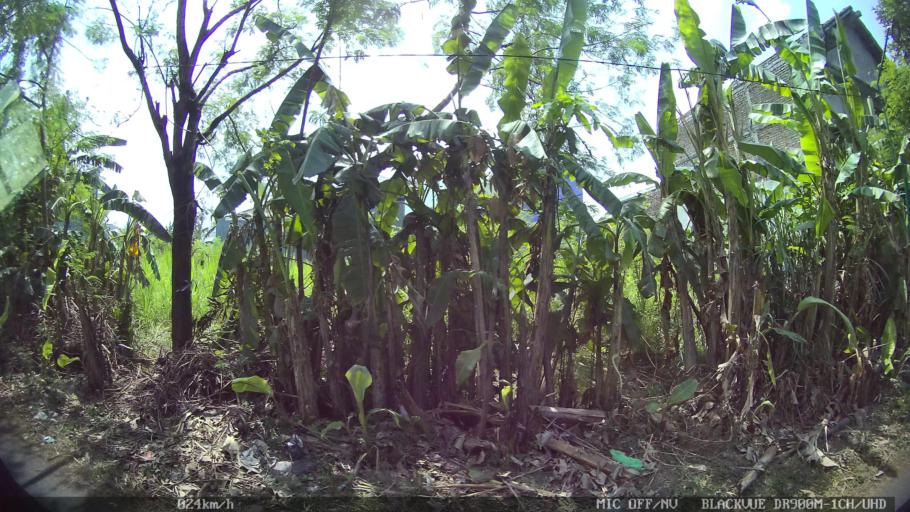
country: ID
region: Daerah Istimewa Yogyakarta
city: Yogyakarta
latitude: -7.8207
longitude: 110.4097
